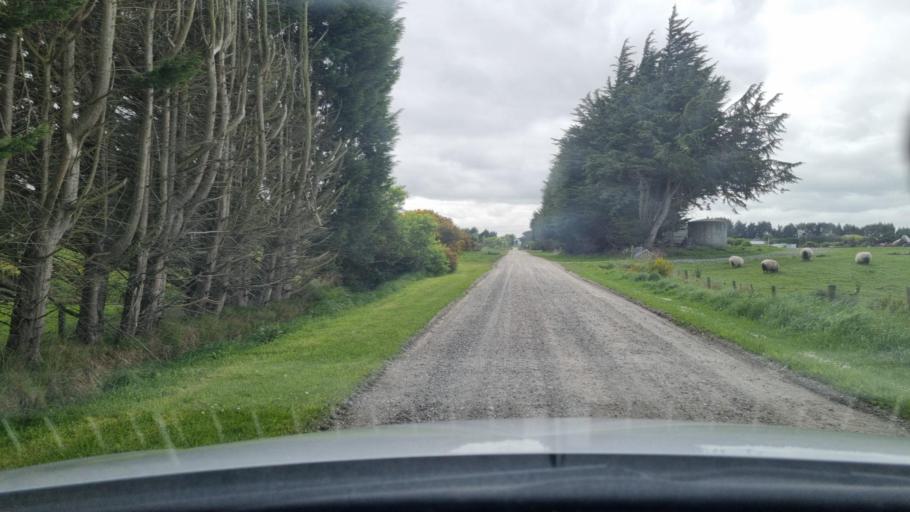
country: NZ
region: Southland
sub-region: Invercargill City
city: Invercargill
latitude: -46.4380
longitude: 168.3897
